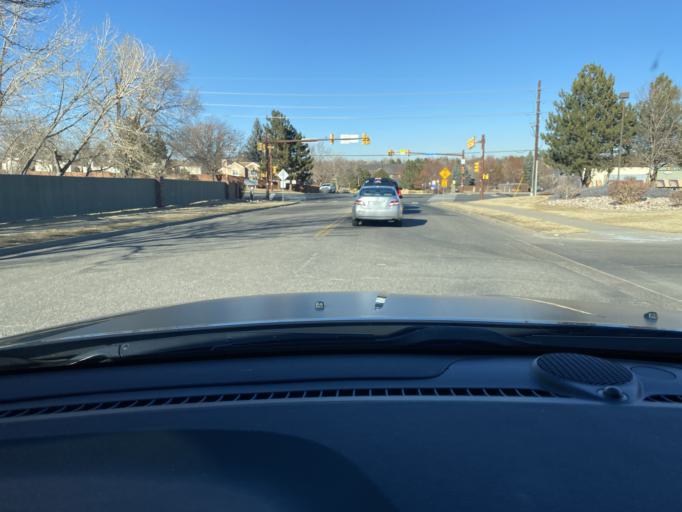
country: US
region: Colorado
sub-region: Jefferson County
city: Arvada
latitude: 39.8120
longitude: -105.1427
